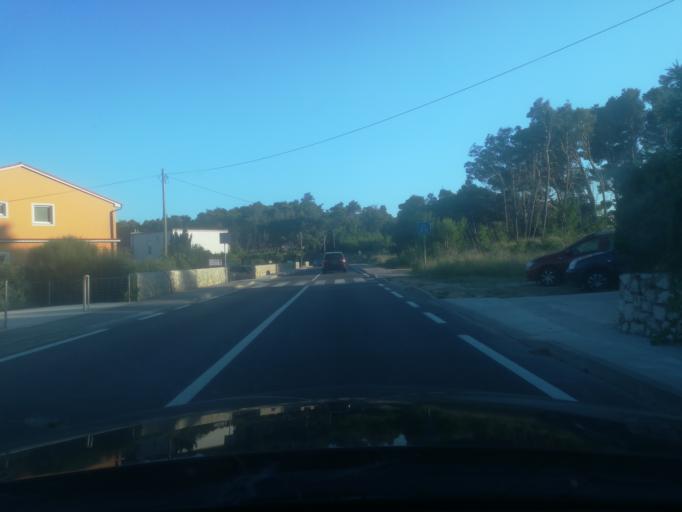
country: HR
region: Primorsko-Goranska
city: Banjol
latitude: 44.7658
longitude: 14.7660
